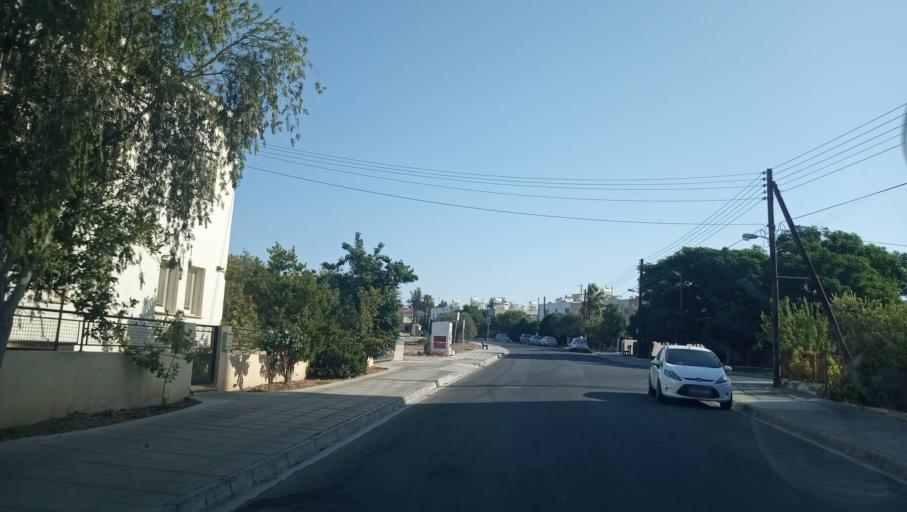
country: CY
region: Lefkosia
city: Nicosia
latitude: 35.1459
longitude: 33.3949
